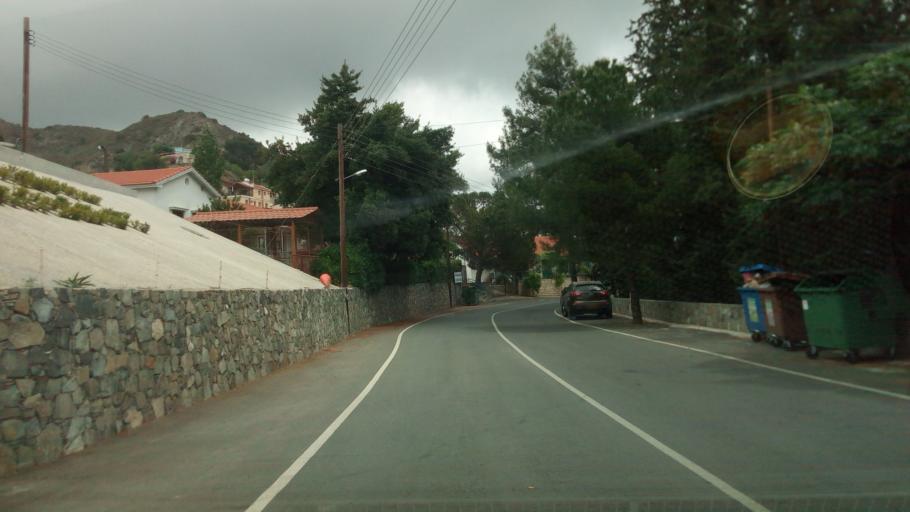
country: CY
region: Limassol
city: Pelendri
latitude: 34.8500
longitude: 33.0293
